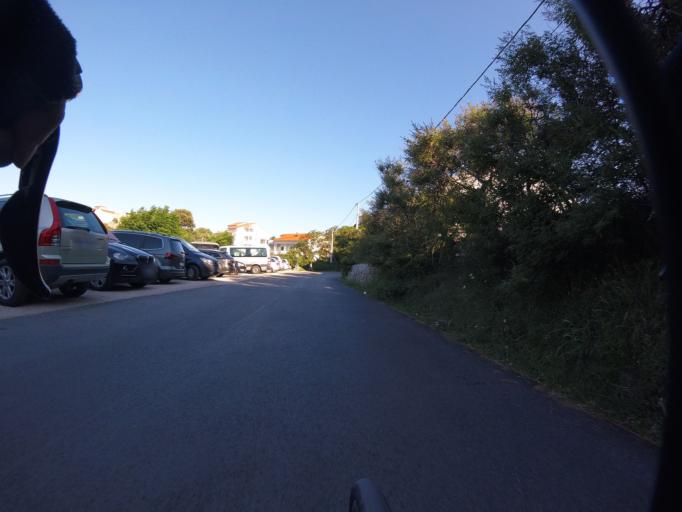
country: HR
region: Primorsko-Goranska
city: Supetarska Draga
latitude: 44.8015
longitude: 14.7119
